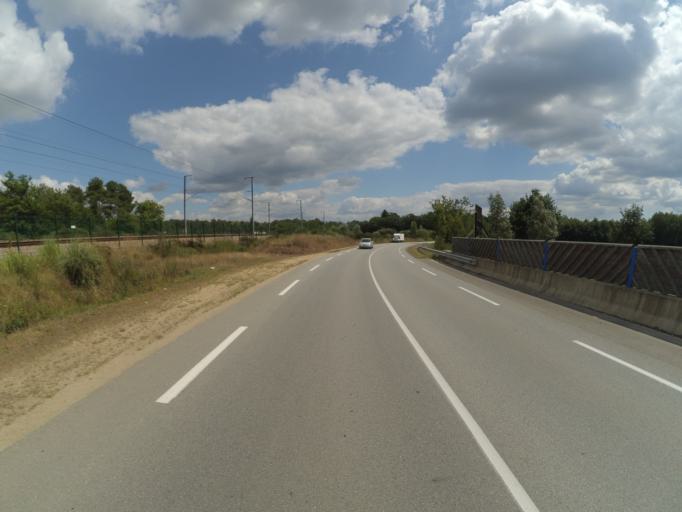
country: FR
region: Brittany
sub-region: Departement du Morbihan
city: Landevant
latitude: 47.7564
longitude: -3.1119
